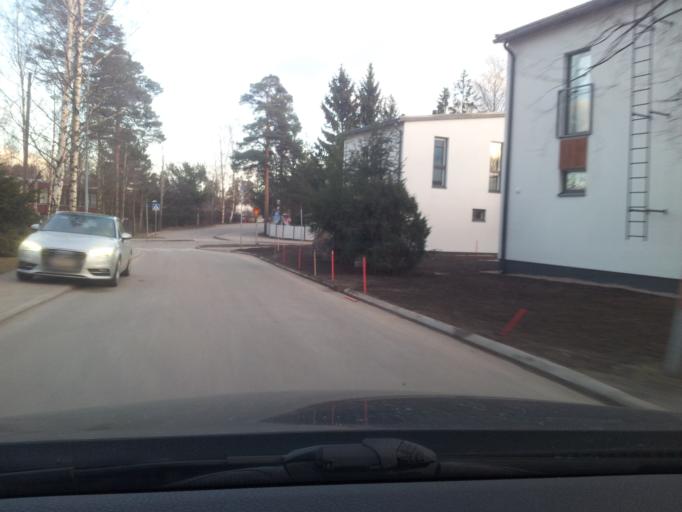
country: FI
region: Uusimaa
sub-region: Helsinki
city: Koukkuniemi
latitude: 60.1769
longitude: 24.7680
